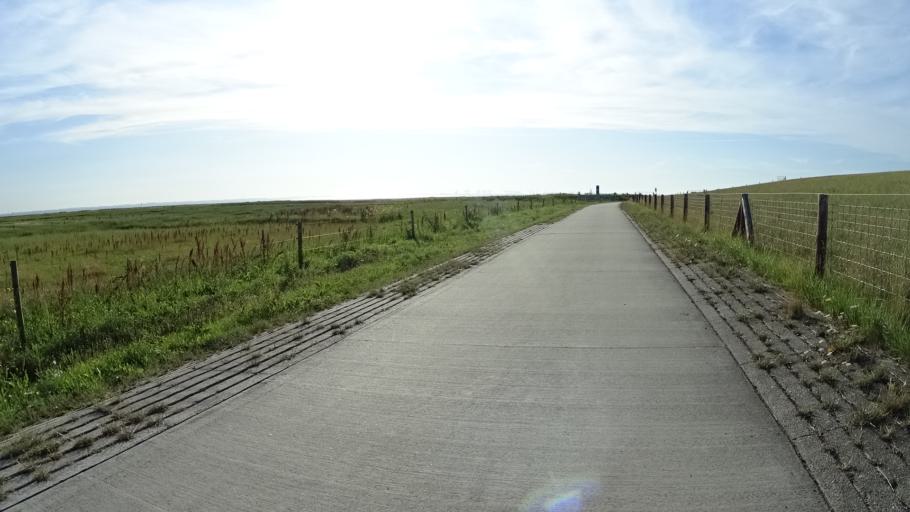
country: DE
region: Lower Saxony
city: Butjadingen
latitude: 53.6039
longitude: 8.3436
